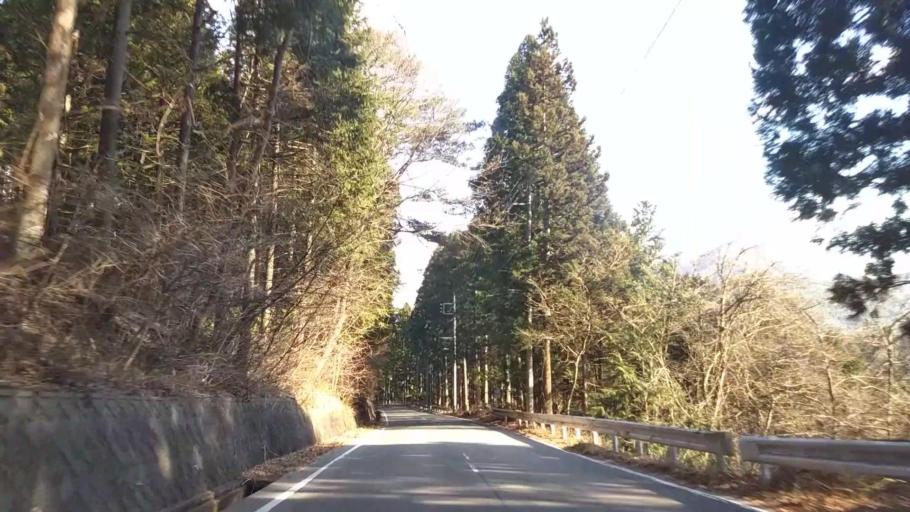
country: JP
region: Yamanashi
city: Otsuki
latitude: 35.5092
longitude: 138.9815
